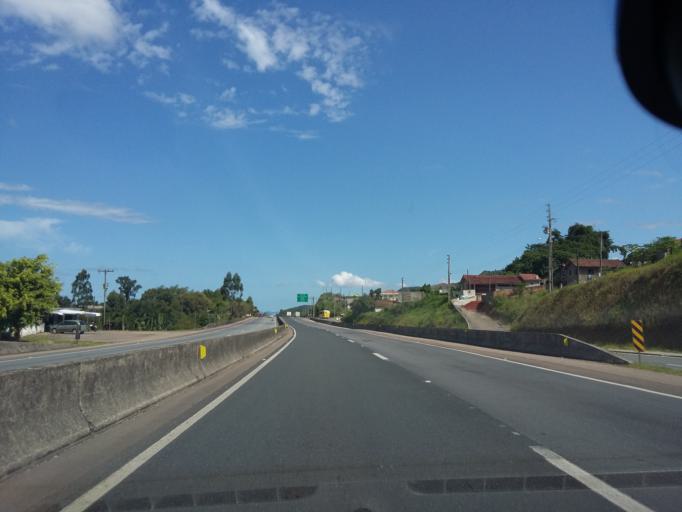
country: BR
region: Santa Catarina
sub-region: Biguacu
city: Biguacu
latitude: -27.3901
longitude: -48.6319
